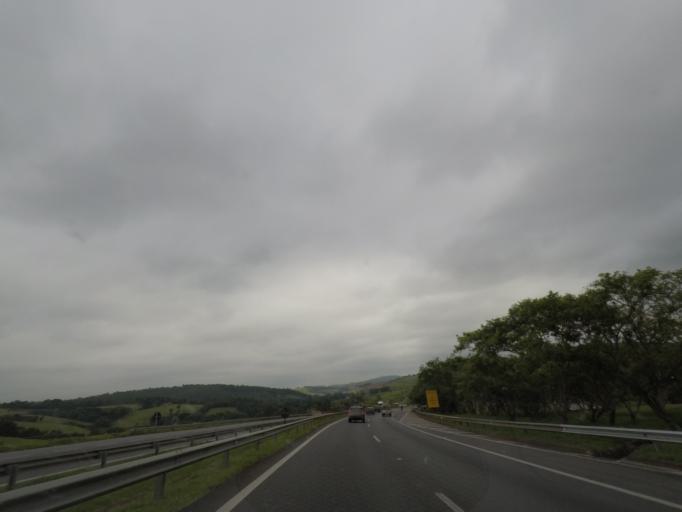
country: BR
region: Sao Paulo
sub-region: Itatiba
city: Itatiba
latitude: -23.0060
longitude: -46.7675
